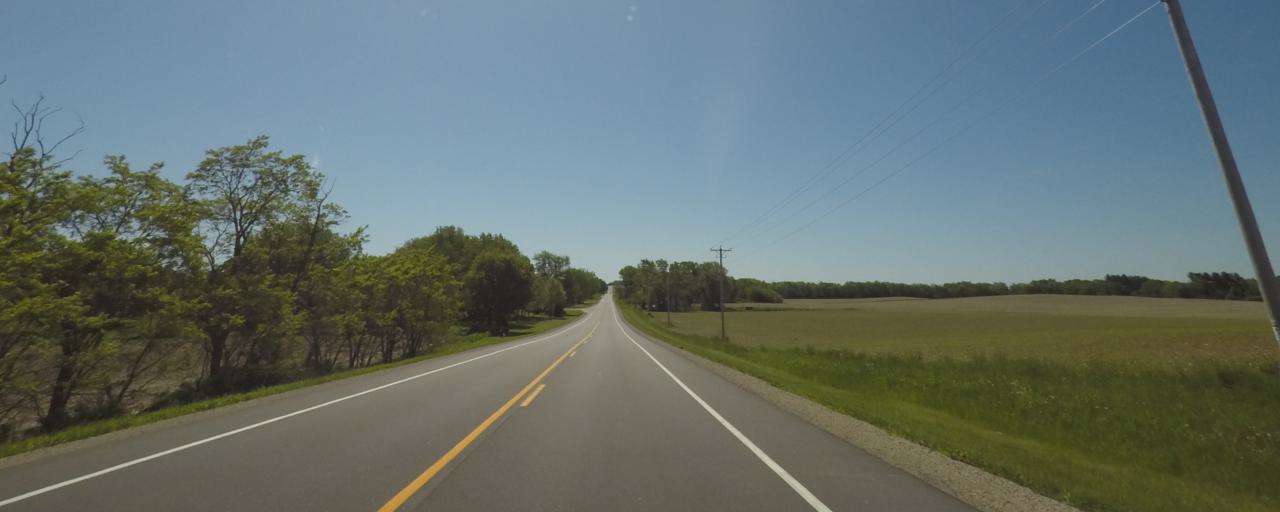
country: US
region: Wisconsin
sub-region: Dane County
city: Fitchburg
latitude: 42.9605
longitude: -89.4794
